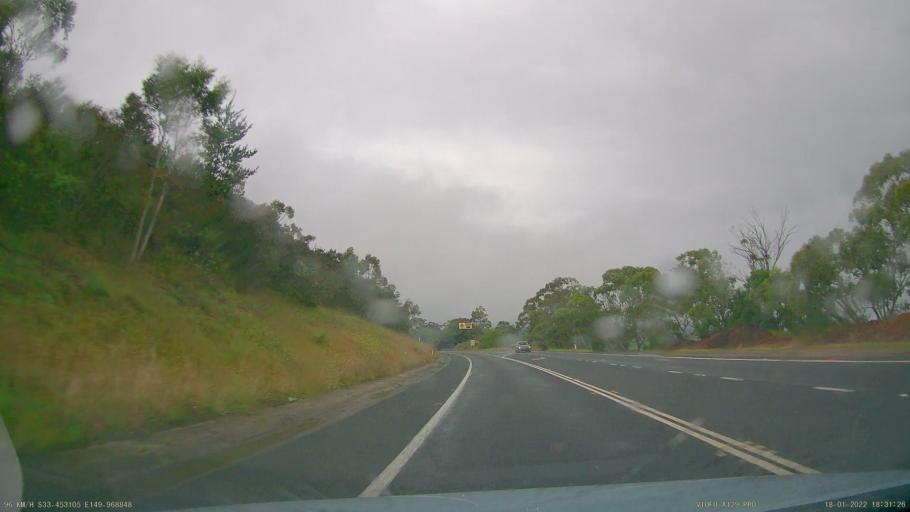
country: AU
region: New South Wales
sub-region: Lithgow
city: Portland
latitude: -33.4532
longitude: 149.9700
